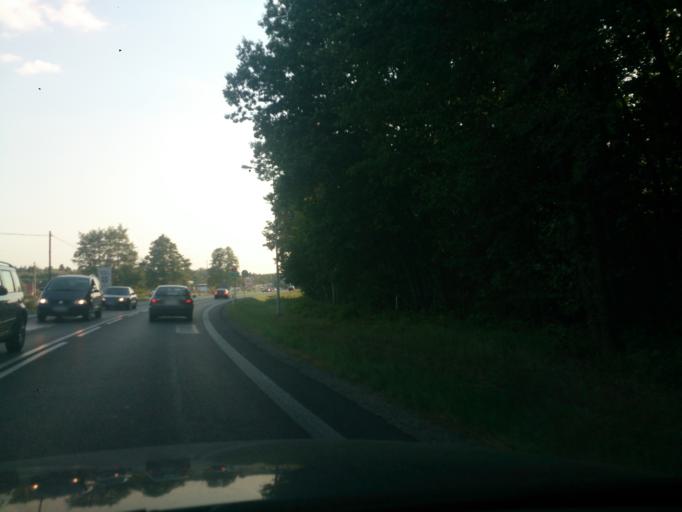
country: PL
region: Subcarpathian Voivodeship
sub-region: Powiat kolbuszowski
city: Majdan Krolewski
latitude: 50.3913
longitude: 21.7618
